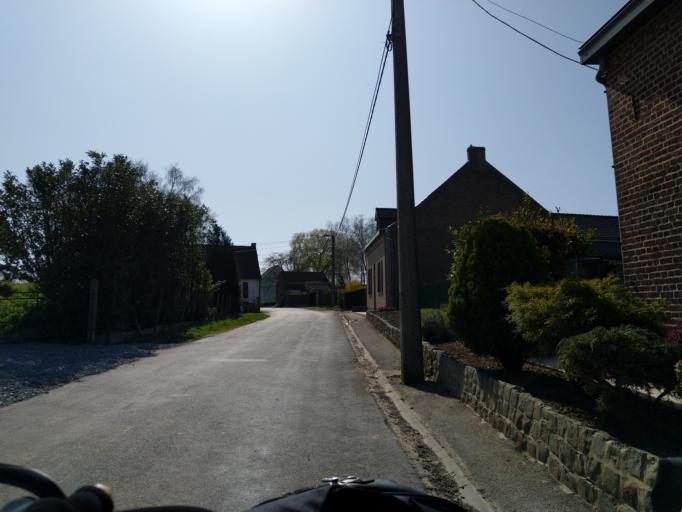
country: BE
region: Wallonia
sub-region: Province du Hainaut
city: Silly
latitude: 50.6954
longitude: 3.8975
